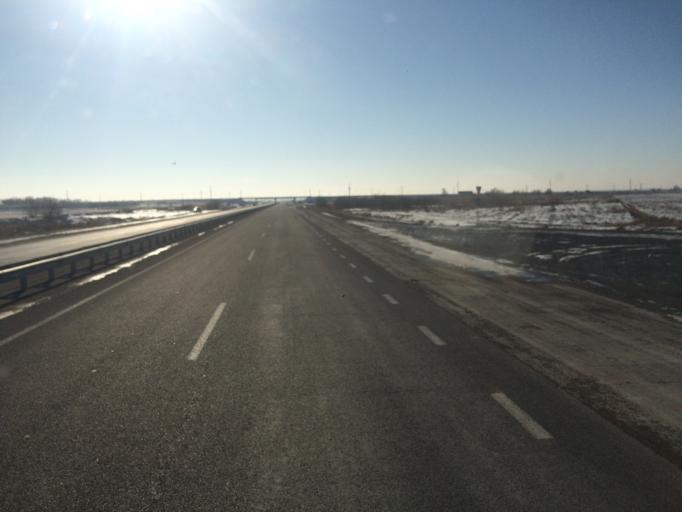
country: KG
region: Chuy
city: Sokuluk
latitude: 43.2812
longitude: 74.2354
